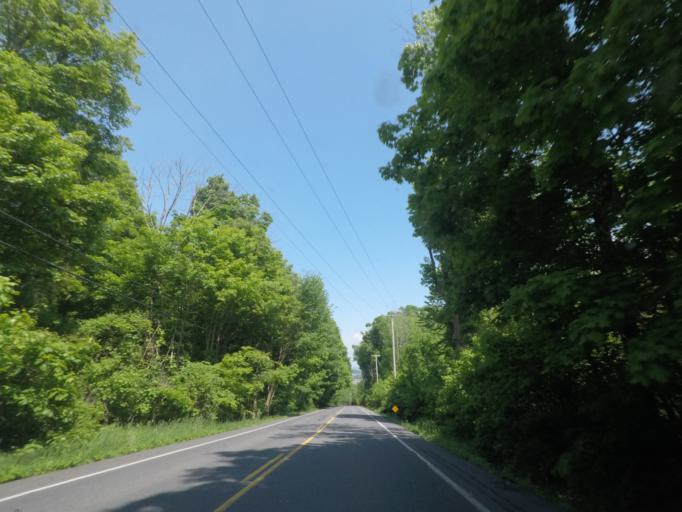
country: US
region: New York
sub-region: Dutchess County
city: Pine Plains
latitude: 41.9682
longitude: -73.5380
